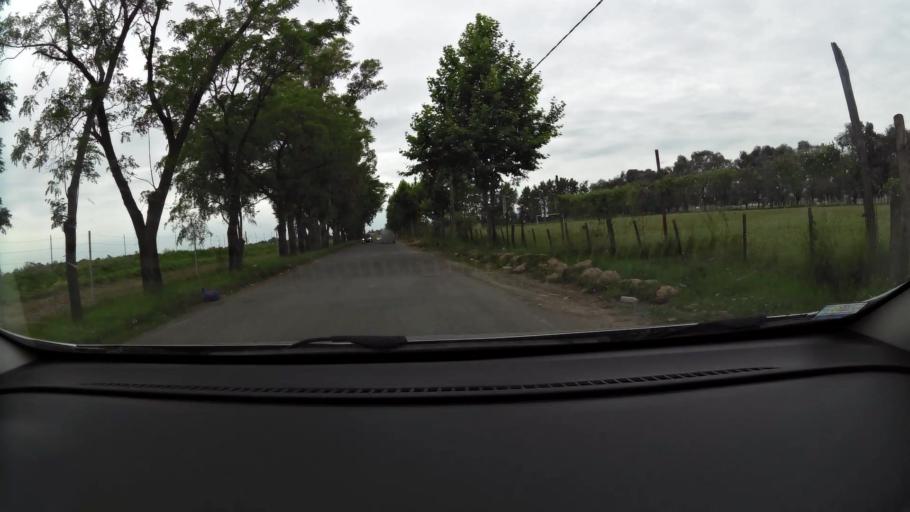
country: AR
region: Buenos Aires
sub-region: Partido de Campana
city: Campana
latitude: -34.2009
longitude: -58.9488
